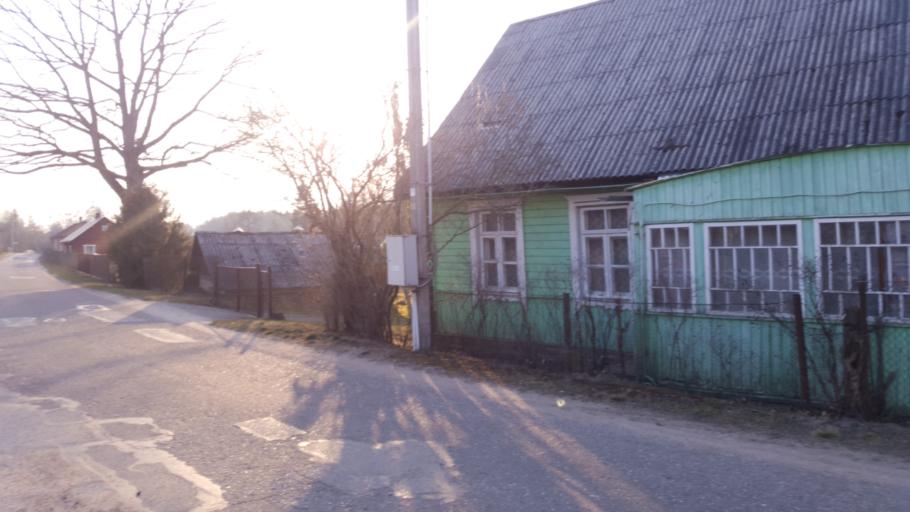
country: LT
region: Alytaus apskritis
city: Varena
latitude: 54.0530
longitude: 24.4065
